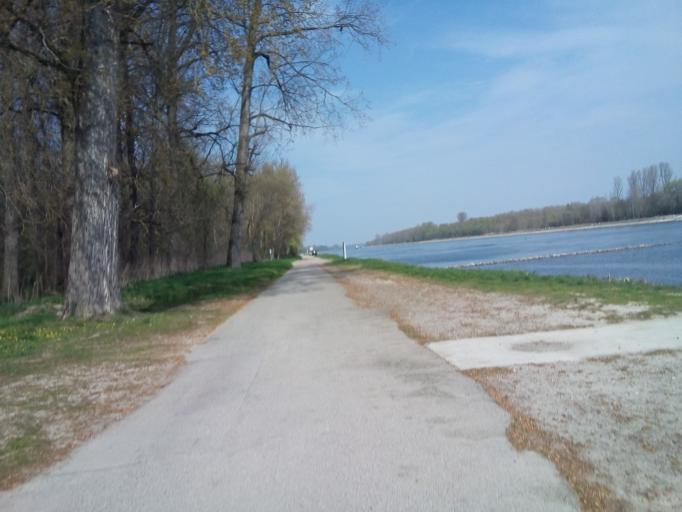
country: DE
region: Baden-Wuerttemberg
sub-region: Karlsruhe Region
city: Iffezheim
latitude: 48.8504
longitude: 8.1127
